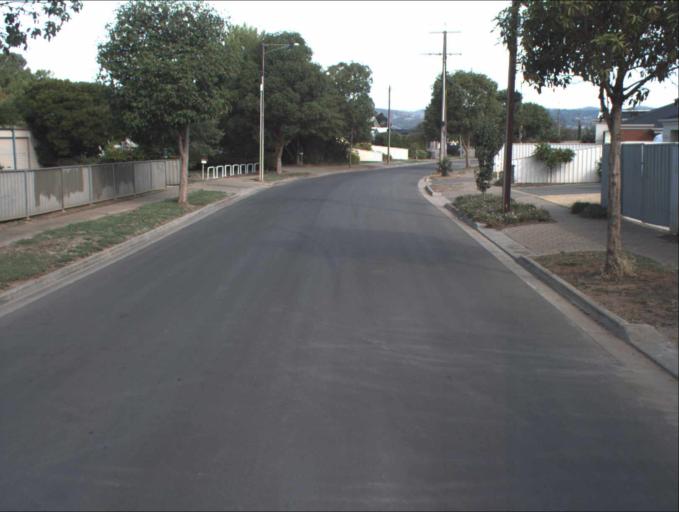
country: AU
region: South Australia
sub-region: Port Adelaide Enfield
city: Gilles Plains
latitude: -34.8680
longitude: 138.6501
